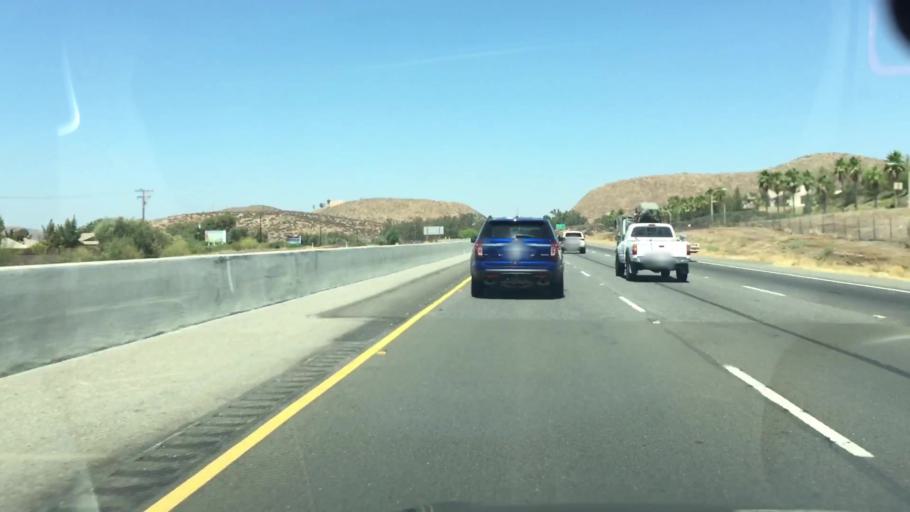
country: US
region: California
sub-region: Riverside County
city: Sun City
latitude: 33.6952
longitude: -117.1774
